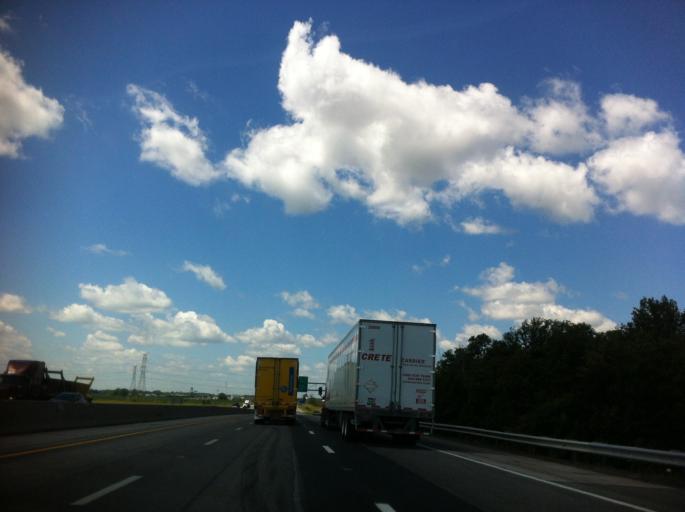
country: US
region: Ohio
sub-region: Wood County
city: Millbury
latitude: 41.5160
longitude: -83.4368
